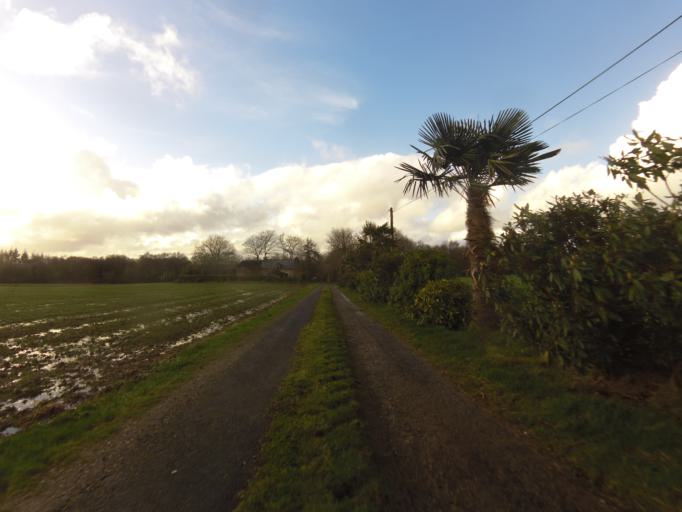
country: FR
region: Brittany
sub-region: Departement des Cotes-d'Armor
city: Gouarec
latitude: 48.1754
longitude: -3.1704
